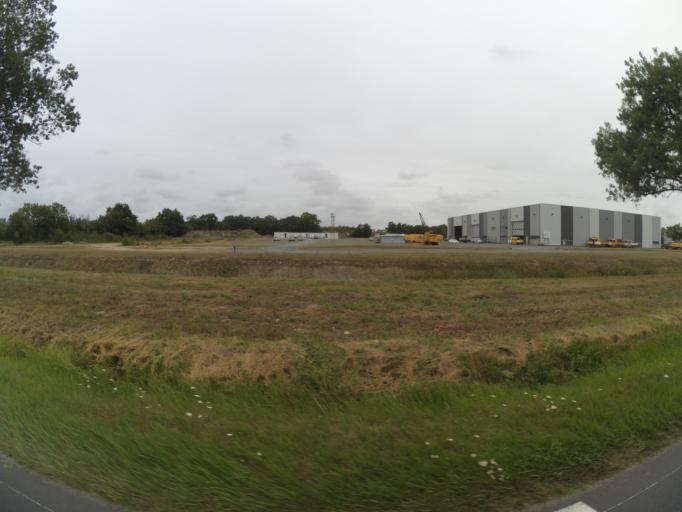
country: FR
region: Pays de la Loire
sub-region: Departement de la Vendee
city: Sallertaine
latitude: 46.8649
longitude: -1.9229
